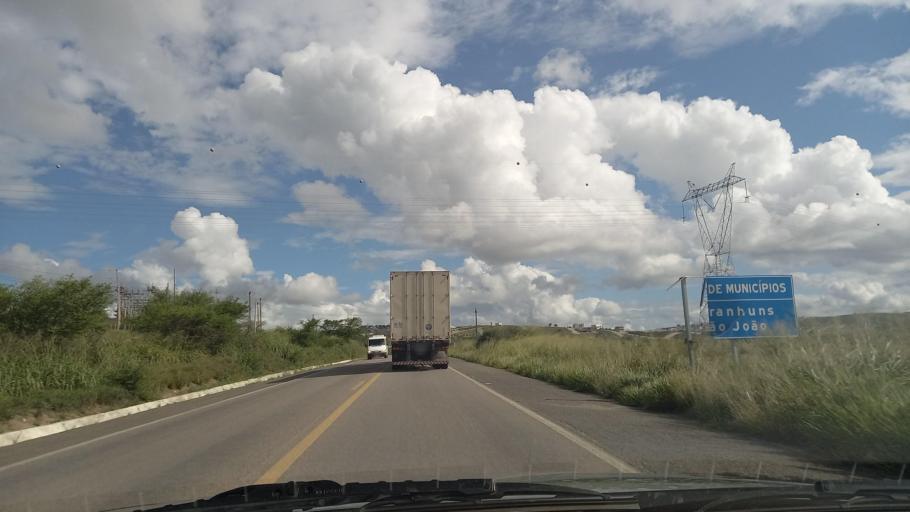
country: BR
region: Pernambuco
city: Garanhuns
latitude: -8.8493
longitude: -36.4611
